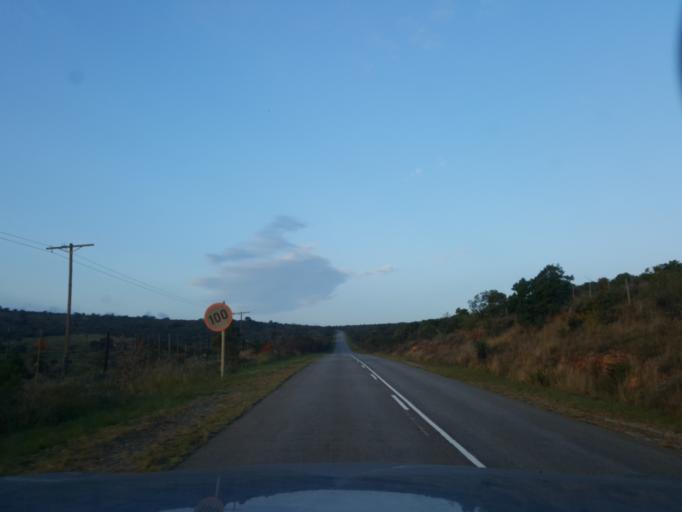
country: ZA
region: Eastern Cape
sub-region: Cacadu District Municipality
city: Grahamstown
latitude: -33.4624
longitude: 26.4848
